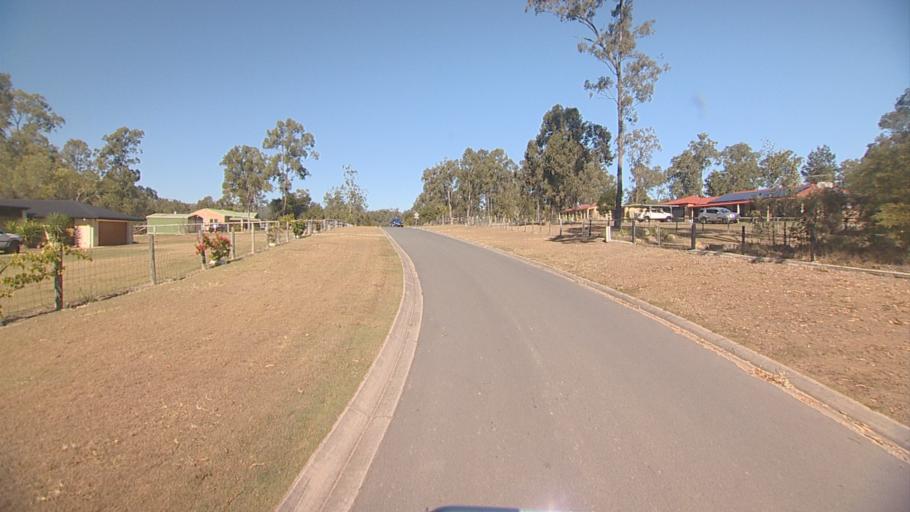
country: AU
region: Queensland
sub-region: Logan
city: North Maclean
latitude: -27.8172
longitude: 152.9590
